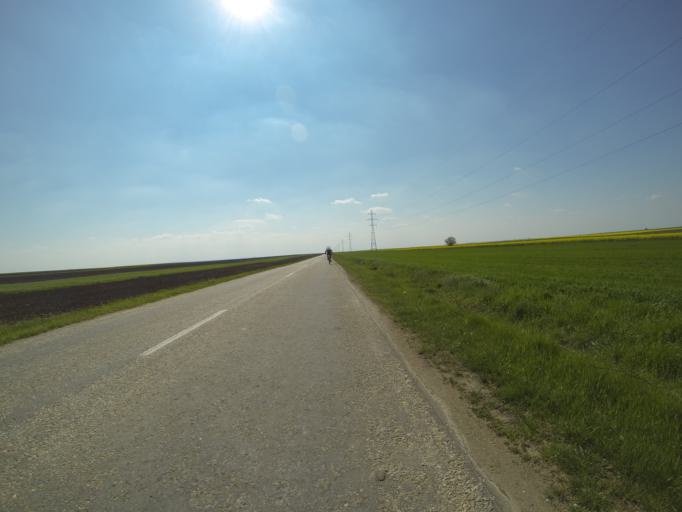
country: RO
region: Dolj
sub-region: Comuna Unirea
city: Unirea
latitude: 44.1620
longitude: 23.1501
